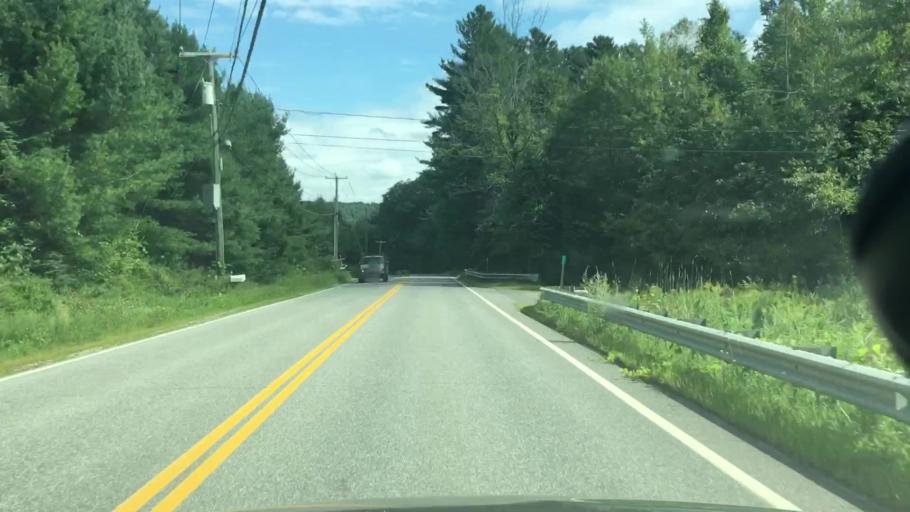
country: US
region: Massachusetts
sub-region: Franklin County
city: Shelburne
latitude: 42.6310
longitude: -72.6685
